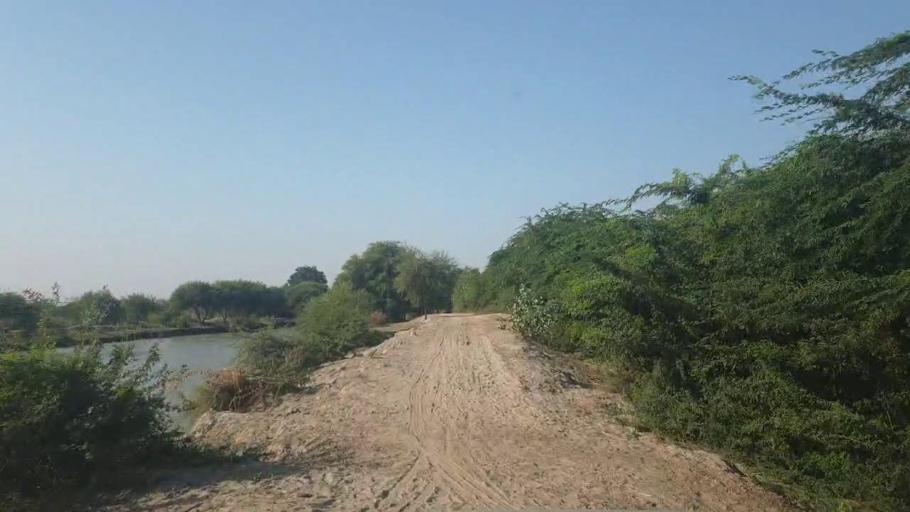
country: PK
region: Sindh
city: Tando Bago
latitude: 24.7187
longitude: 68.9156
